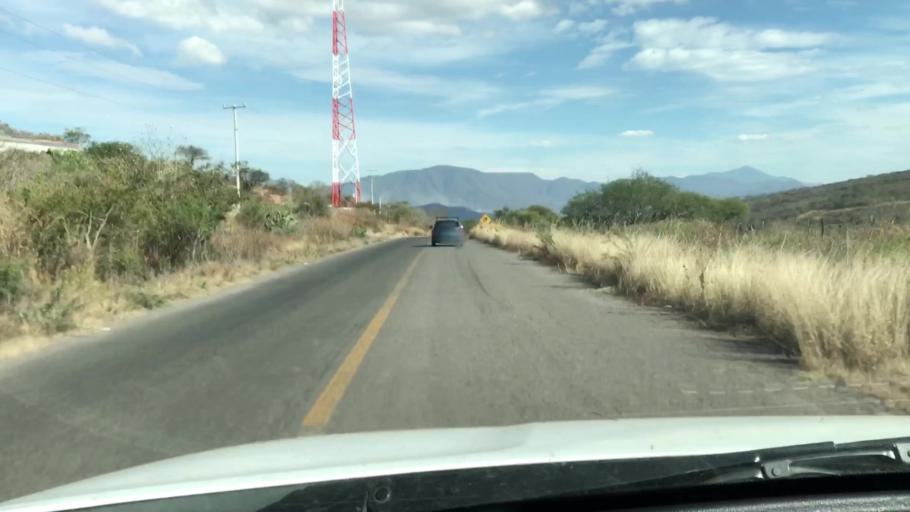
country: MX
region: Jalisco
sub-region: Zacoalco de Torres
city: Barranca de Otates (Barranca de Otatan)
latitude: 20.2588
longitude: -103.6591
